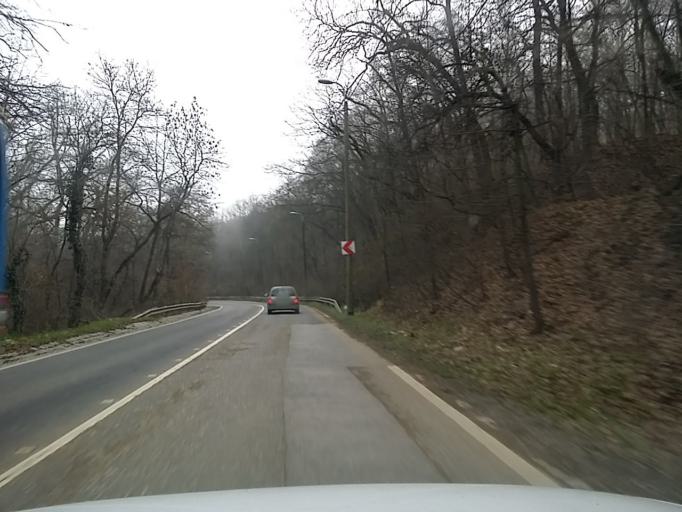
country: HU
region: Pest
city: Budakeszi
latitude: 47.5433
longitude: 18.9453
